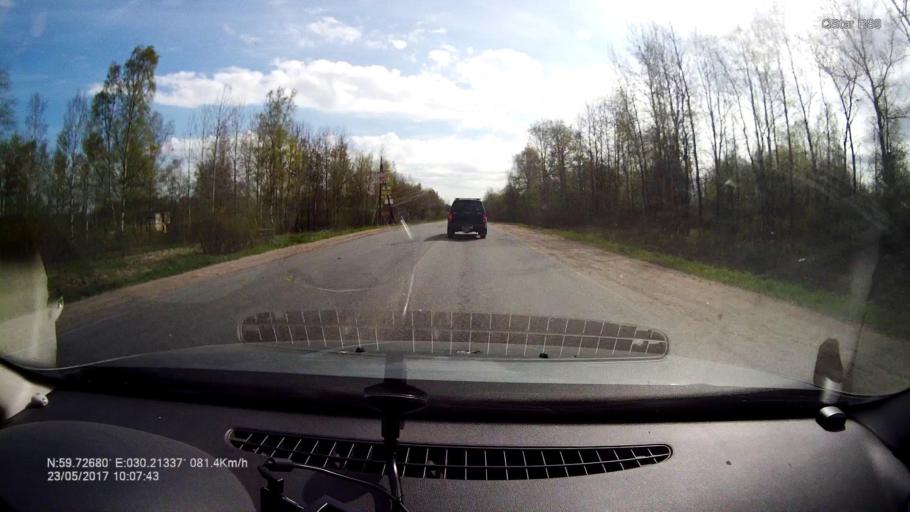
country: RU
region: St.-Petersburg
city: Gorelovo
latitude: 59.7268
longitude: 30.2138
